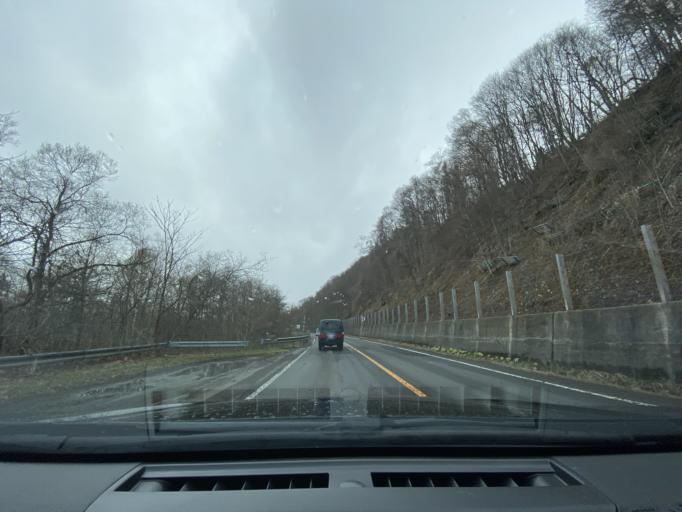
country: JP
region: Hokkaido
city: Fukagawa
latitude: 43.7032
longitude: 142.0829
